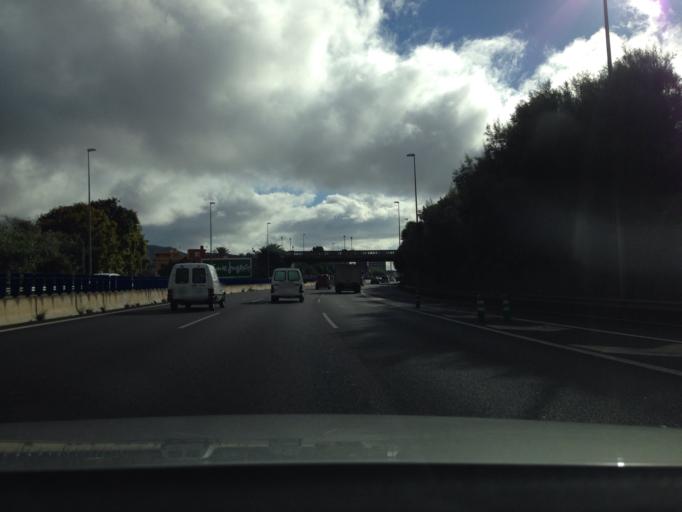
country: ES
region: Canary Islands
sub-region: Provincia de Santa Cruz de Tenerife
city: La Laguna
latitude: 28.4896
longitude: -16.3351
